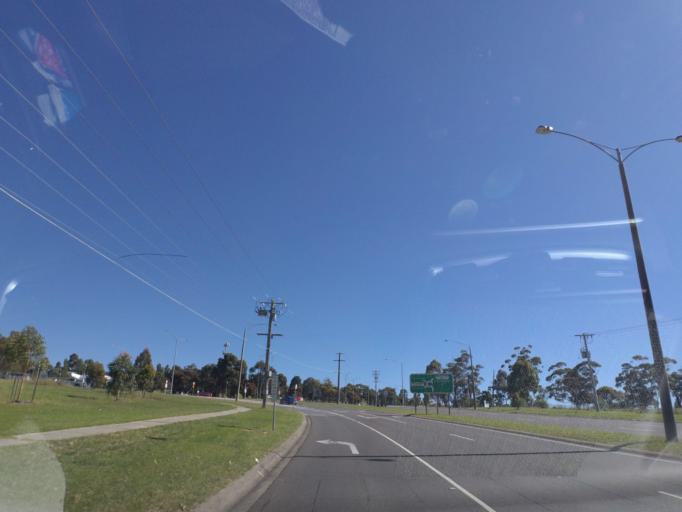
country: AU
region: Victoria
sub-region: Banyule
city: Greensborough
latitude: -37.6905
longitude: 145.1138
